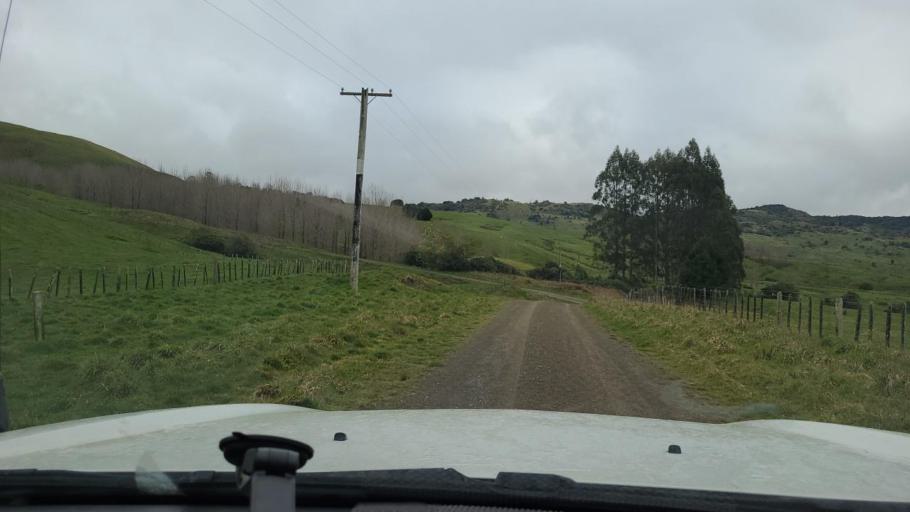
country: NZ
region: Hawke's Bay
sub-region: Wairoa District
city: Wairoa
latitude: -38.5385
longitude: 177.4214
